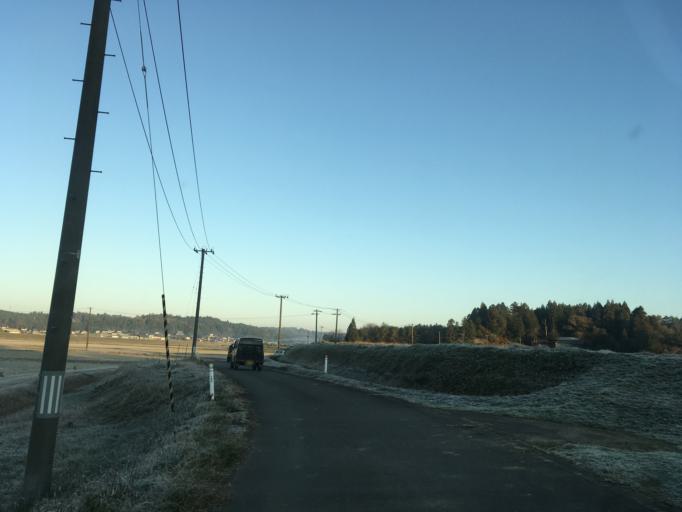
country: JP
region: Iwate
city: Ichinoseki
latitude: 38.7944
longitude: 141.1849
